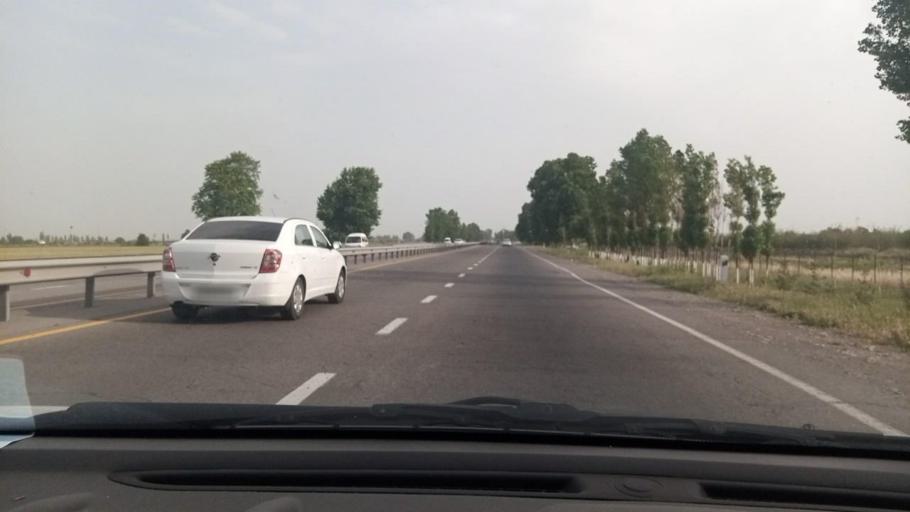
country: UZ
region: Toshkent Shahri
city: Bektemir
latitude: 41.1973
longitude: 69.4030
